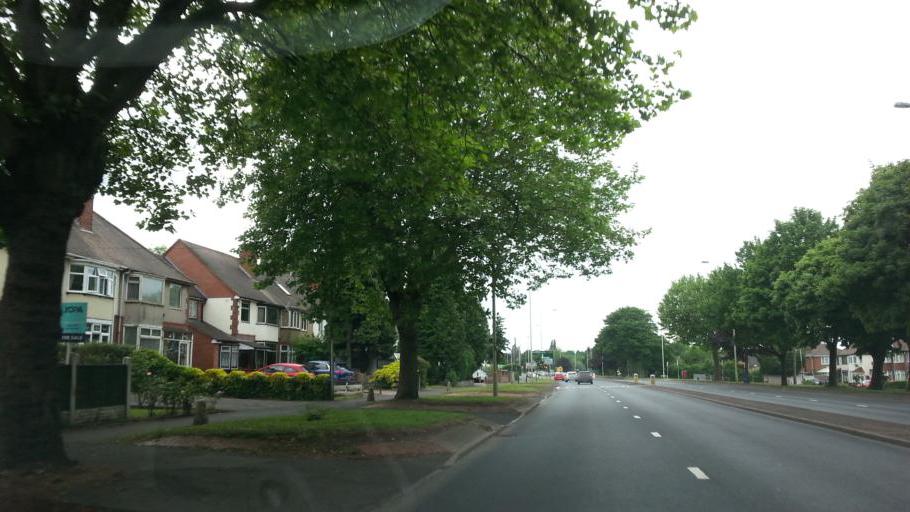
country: GB
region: England
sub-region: Sandwell
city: Tipton
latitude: 52.5215
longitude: -2.0710
